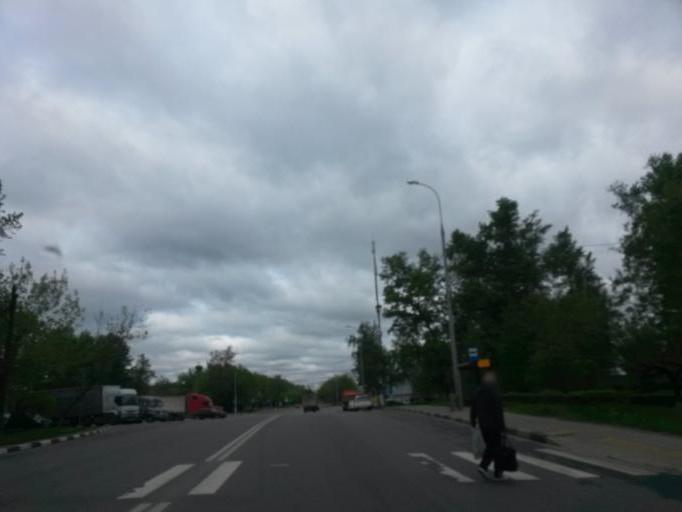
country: RU
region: Moscow
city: Kapotnya
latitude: 55.6422
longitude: 37.7977
